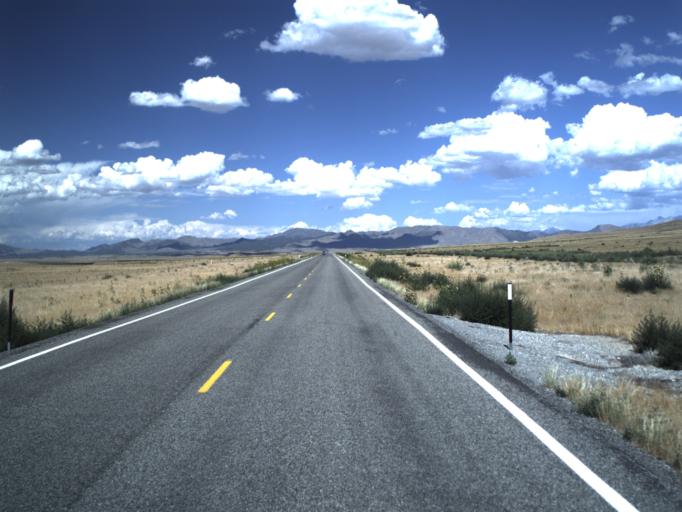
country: US
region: Utah
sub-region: Millard County
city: Delta
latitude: 39.6567
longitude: -112.2863
